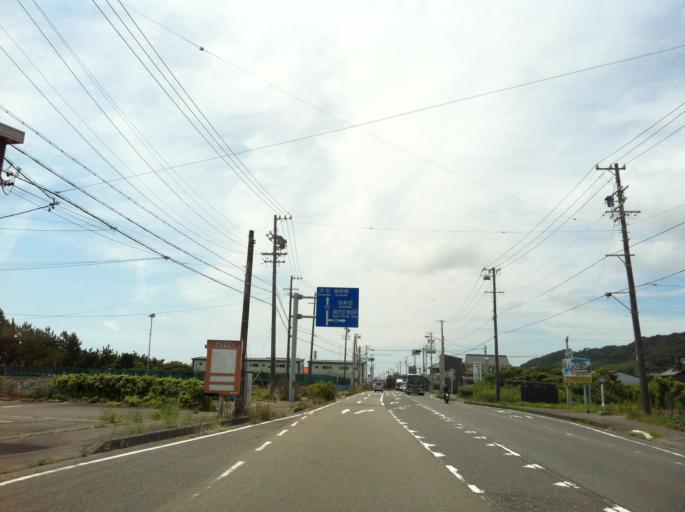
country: JP
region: Shizuoka
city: Sagara
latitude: 34.6645
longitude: 138.1938
